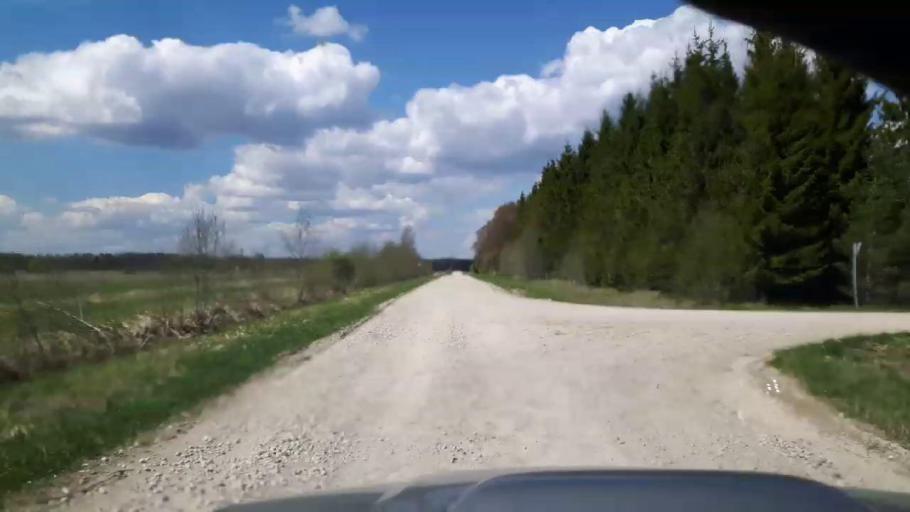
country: EE
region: Paernumaa
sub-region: Tootsi vald
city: Tootsi
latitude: 58.4599
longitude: 24.8778
